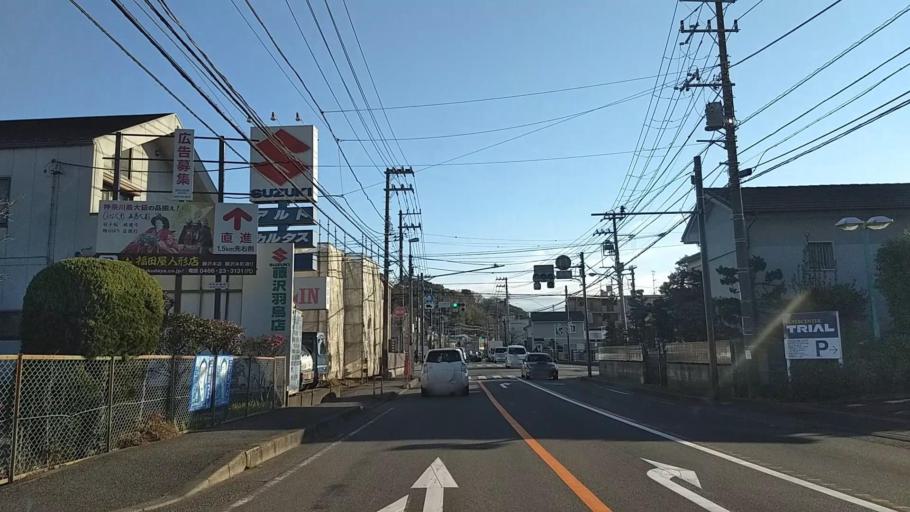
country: JP
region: Kanagawa
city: Fujisawa
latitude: 35.3474
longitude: 139.4657
